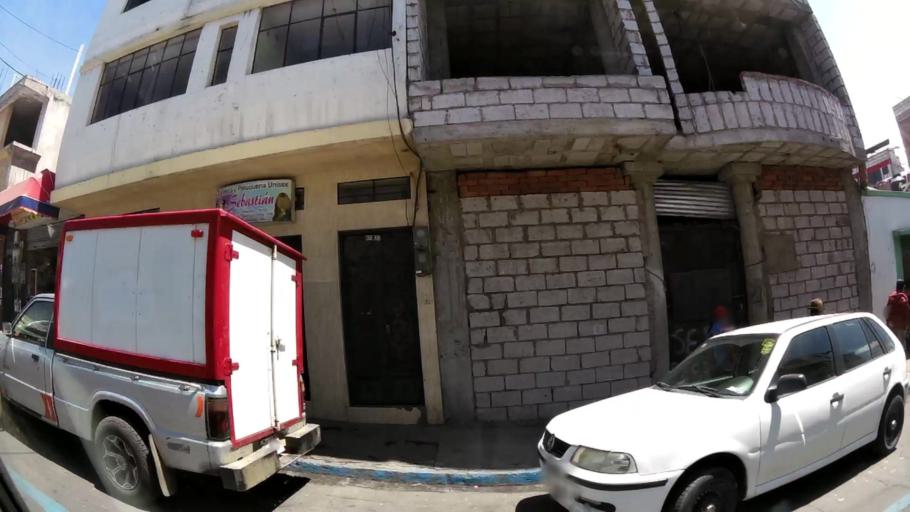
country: EC
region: Chimborazo
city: Riobamba
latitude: -1.6708
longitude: -78.6555
